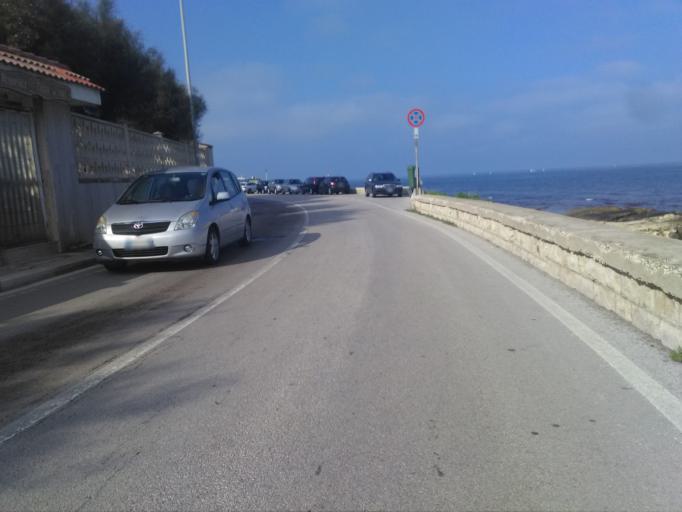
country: IT
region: Apulia
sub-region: Provincia di Bari
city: San Paolo
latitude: 41.1623
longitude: 16.7615
